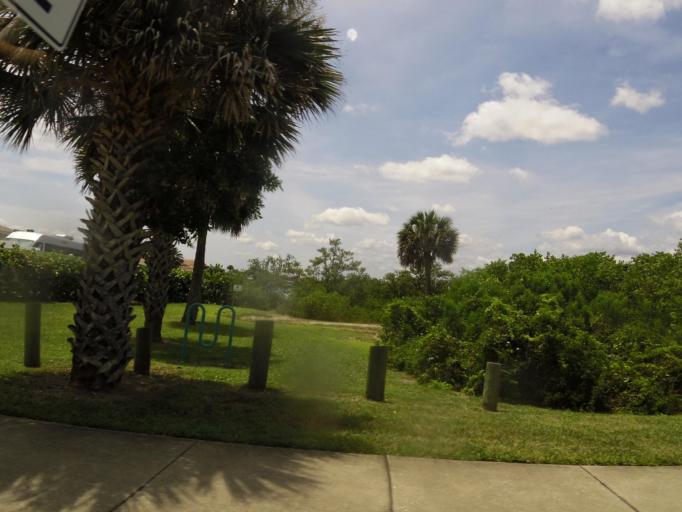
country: US
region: Florida
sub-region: Volusia County
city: Ponce Inlet
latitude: 29.1194
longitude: -80.9531
